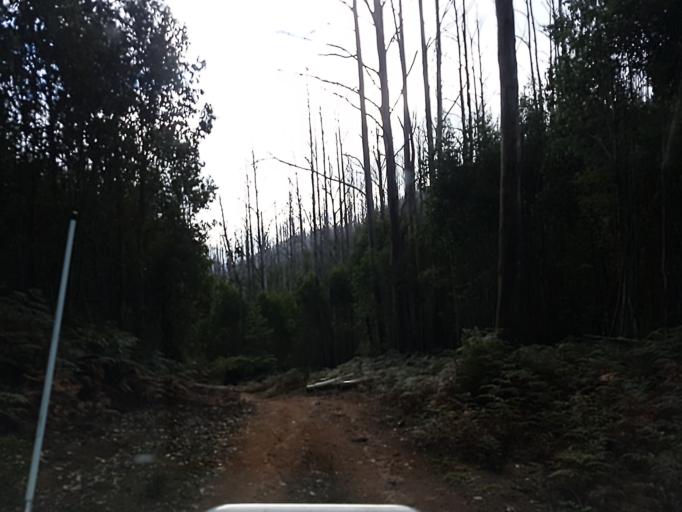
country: AU
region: Victoria
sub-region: Yarra Ranges
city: Millgrove
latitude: -37.5661
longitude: 145.7569
